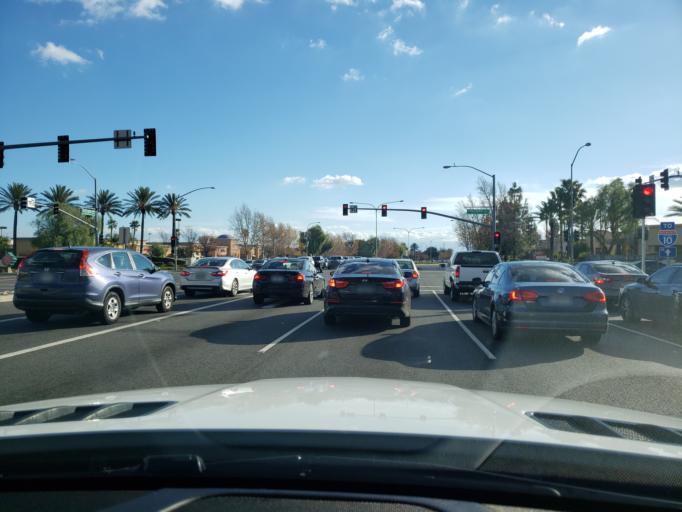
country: US
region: California
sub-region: San Bernardino County
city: Rancho Cucamonga
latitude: 34.0749
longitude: -117.5578
